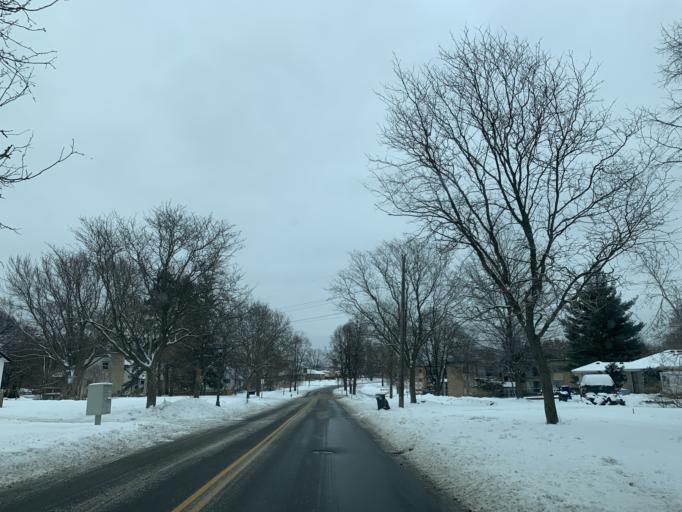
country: US
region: Minnesota
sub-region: Ramsey County
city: Little Canada
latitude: 44.9890
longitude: -93.1108
